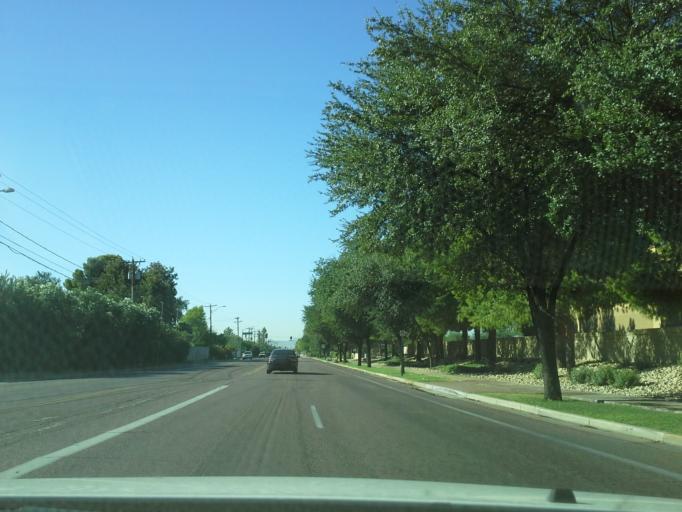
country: US
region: Arizona
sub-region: Maricopa County
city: Phoenix
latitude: 33.5223
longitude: -112.0912
